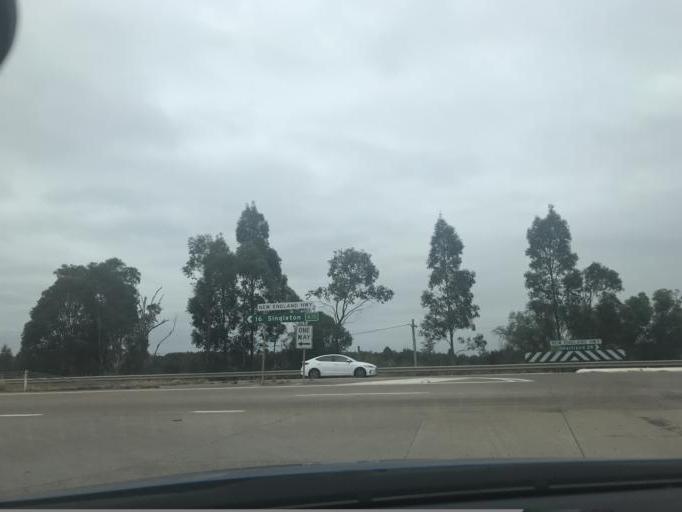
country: AU
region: New South Wales
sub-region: Cessnock
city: Branxton
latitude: -32.6540
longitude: 151.2750
